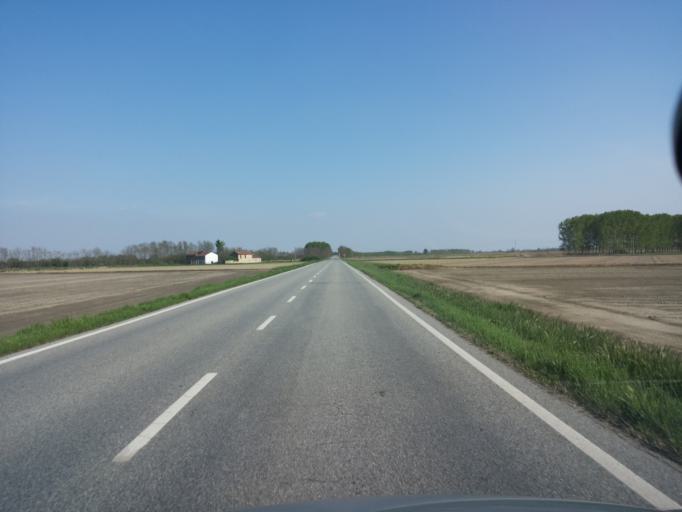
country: IT
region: Piedmont
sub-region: Provincia di Vercelli
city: Motta De Conti
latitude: 45.2089
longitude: 8.5267
